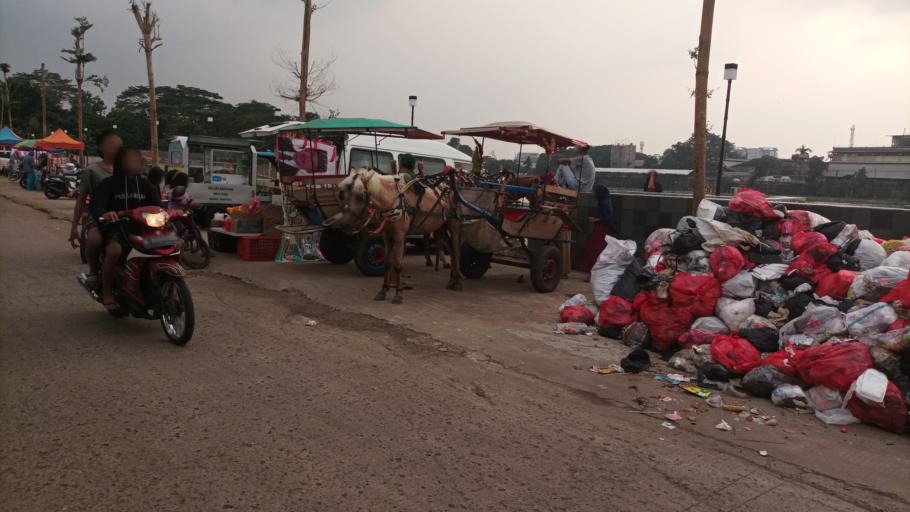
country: ID
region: West Java
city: Depok
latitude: -6.3945
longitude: 106.8694
